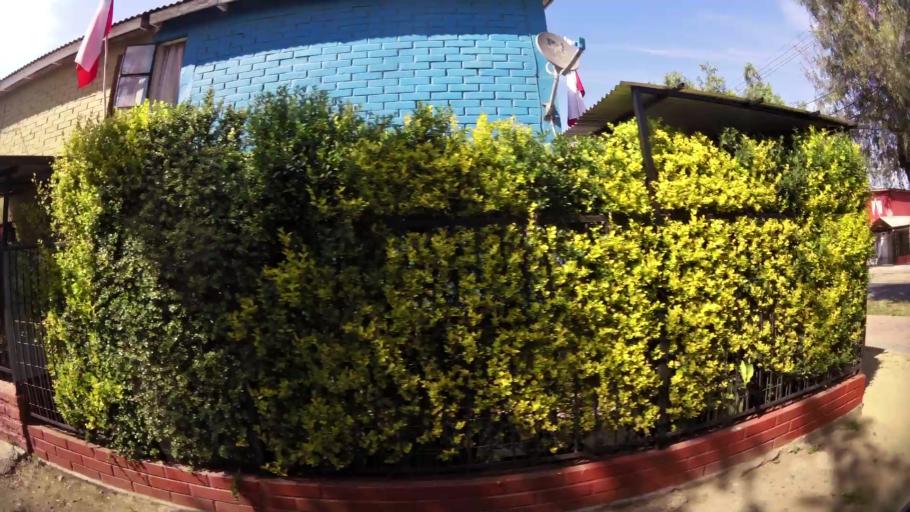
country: CL
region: Santiago Metropolitan
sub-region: Provincia de Talagante
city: Talagante
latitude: -33.6780
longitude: -70.9494
